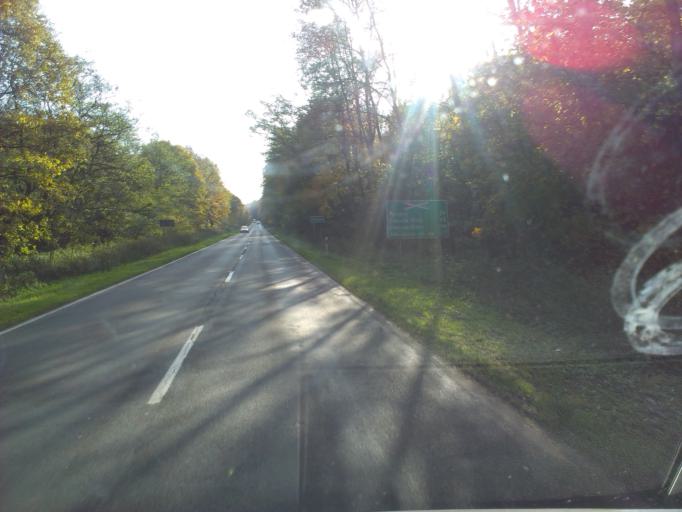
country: PL
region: West Pomeranian Voivodeship
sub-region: Powiat gryfinski
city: Stare Czarnowo
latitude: 53.3403
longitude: 14.7616
